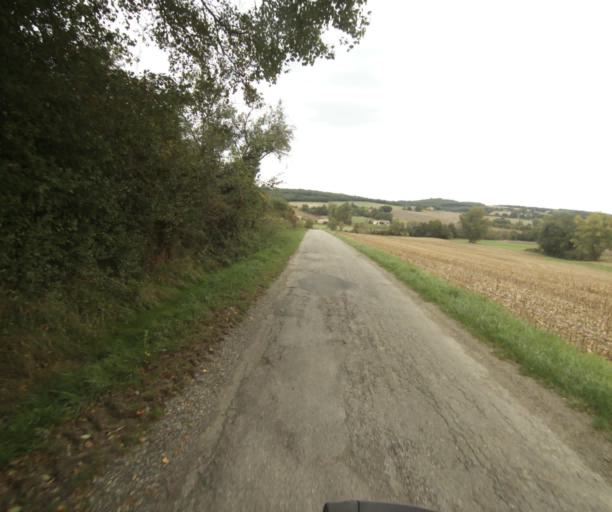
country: FR
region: Midi-Pyrenees
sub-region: Departement du Tarn-et-Garonne
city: Beaumont-de-Lomagne
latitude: 43.8486
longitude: 1.0879
